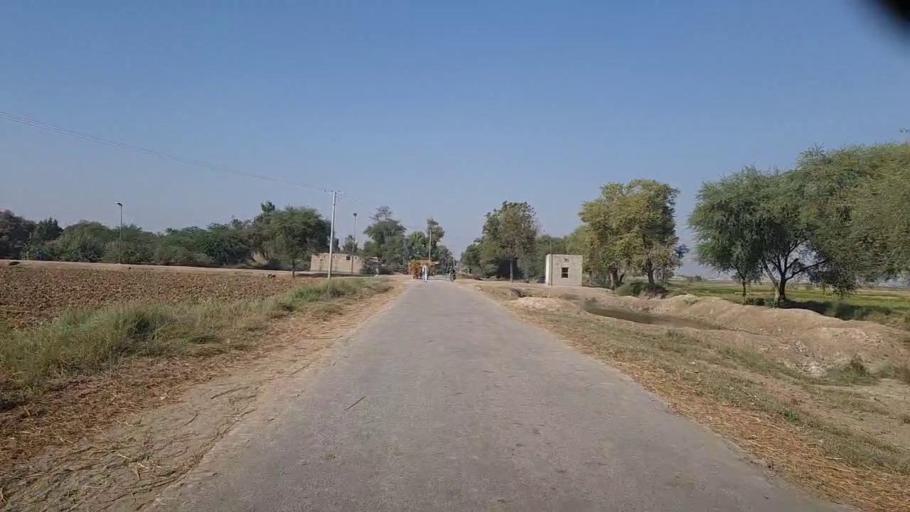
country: PK
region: Sindh
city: Tangwani
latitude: 28.2446
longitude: 68.9965
